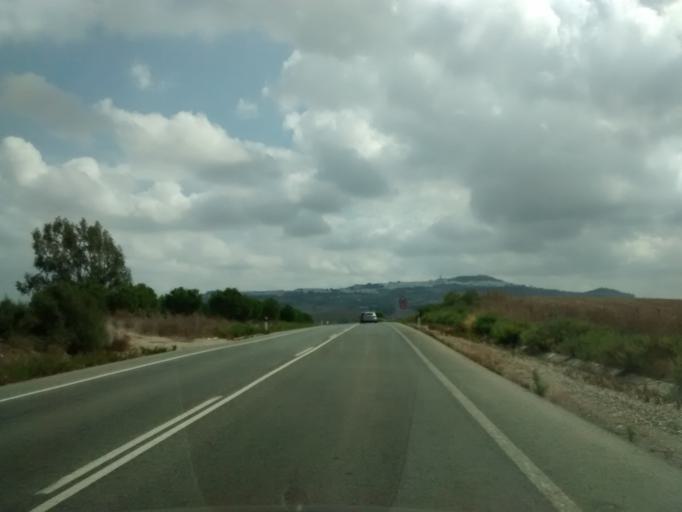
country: ES
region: Andalusia
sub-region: Provincia de Cadiz
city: Medina Sidonia
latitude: 36.4540
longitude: -5.9699
